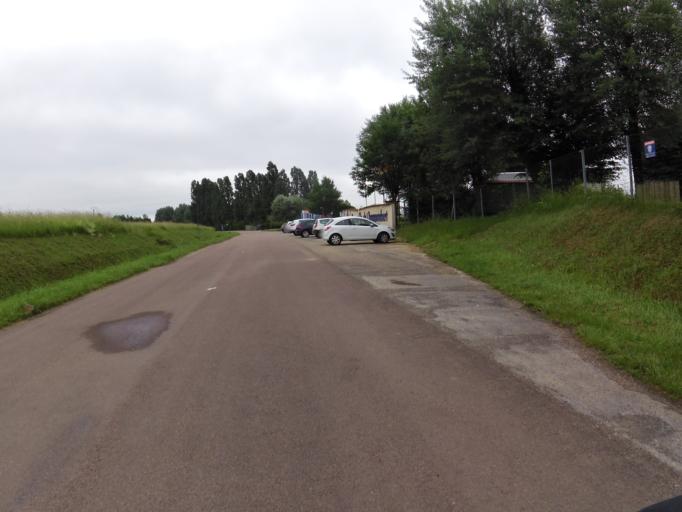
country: FR
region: Champagne-Ardenne
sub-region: Departement de la Haute-Marne
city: Montier-en-Der
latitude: 48.5546
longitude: 4.7924
